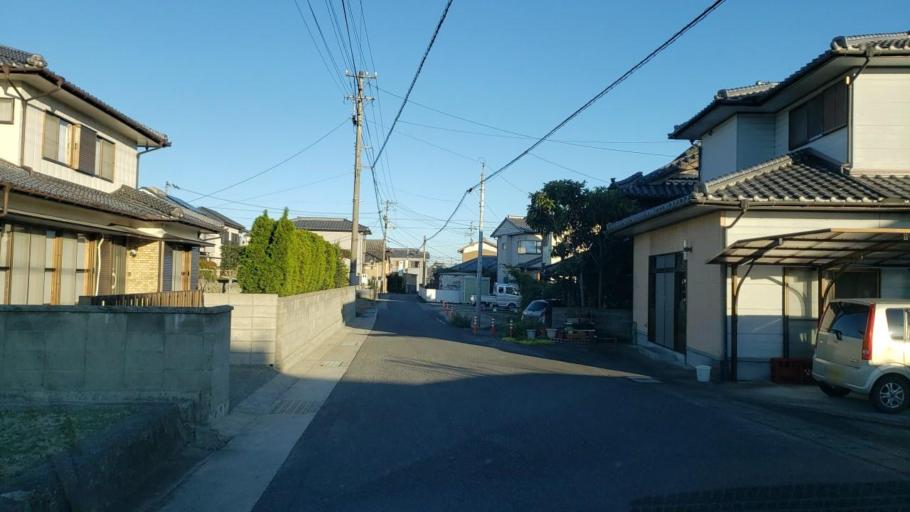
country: JP
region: Tokushima
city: Wakimachi
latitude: 34.0918
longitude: 134.2424
